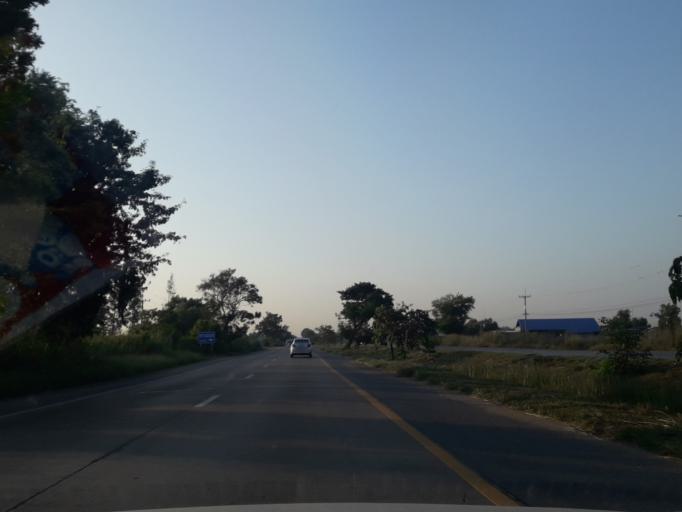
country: TH
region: Phra Nakhon Si Ayutthaya
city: Bang Pa-in
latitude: 14.2570
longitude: 100.5349
